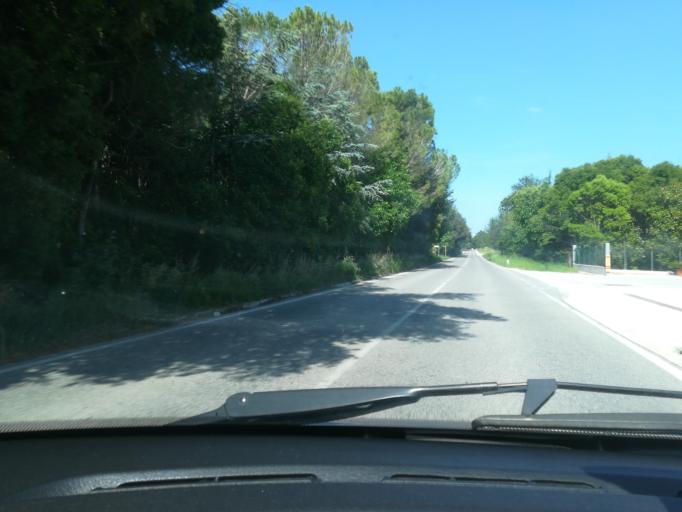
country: IT
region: The Marches
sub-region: Provincia di Macerata
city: Passo di Treia
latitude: 43.2837
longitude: 13.3415
